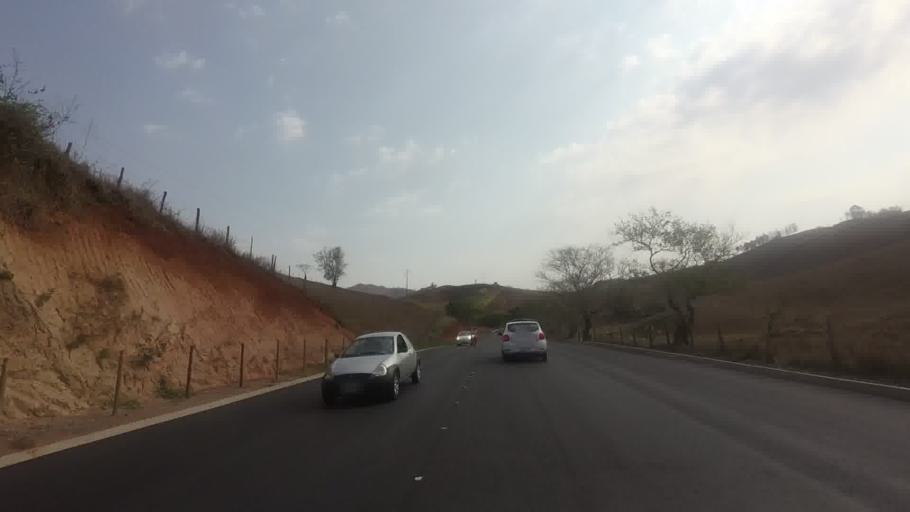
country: BR
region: Rio de Janeiro
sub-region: Bom Jesus Do Itabapoana
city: Bom Jesus do Itabapoana
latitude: -21.1971
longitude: -41.7103
